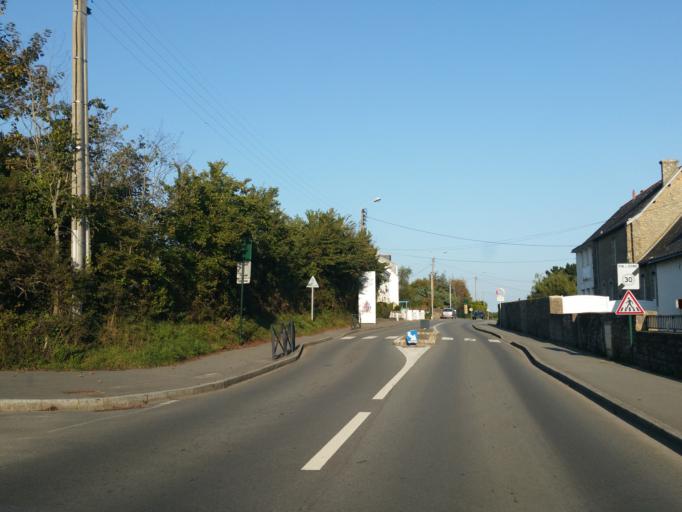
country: FR
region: Brittany
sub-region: Departement du Morbihan
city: Carnac
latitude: 47.5856
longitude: -3.0749
